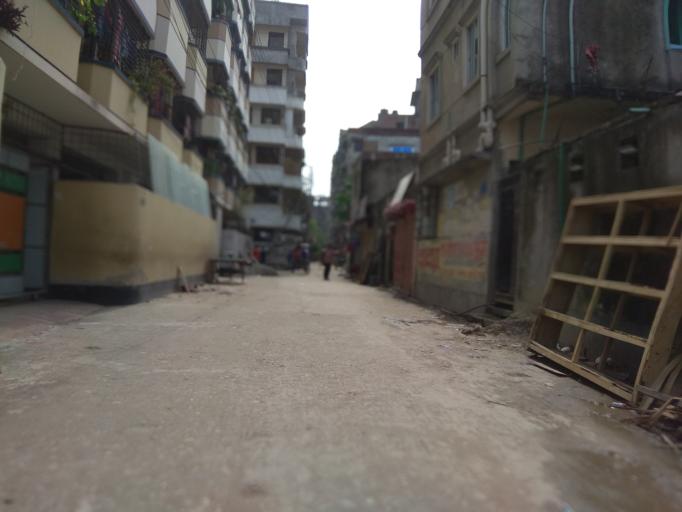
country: BD
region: Dhaka
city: Azimpur
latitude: 23.7977
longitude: 90.3578
